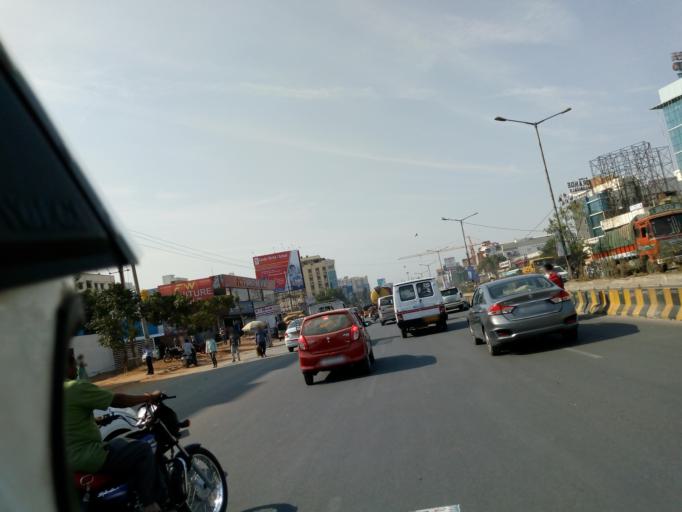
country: IN
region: Telangana
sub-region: Rangareddi
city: Lal Bahadur Nagar
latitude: 17.3439
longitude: 78.5546
